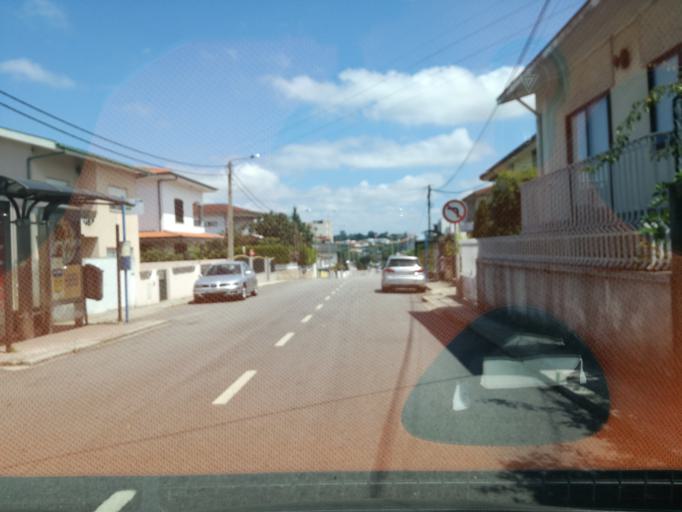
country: PT
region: Porto
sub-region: Maia
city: Maia
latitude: 41.2351
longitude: -8.6100
